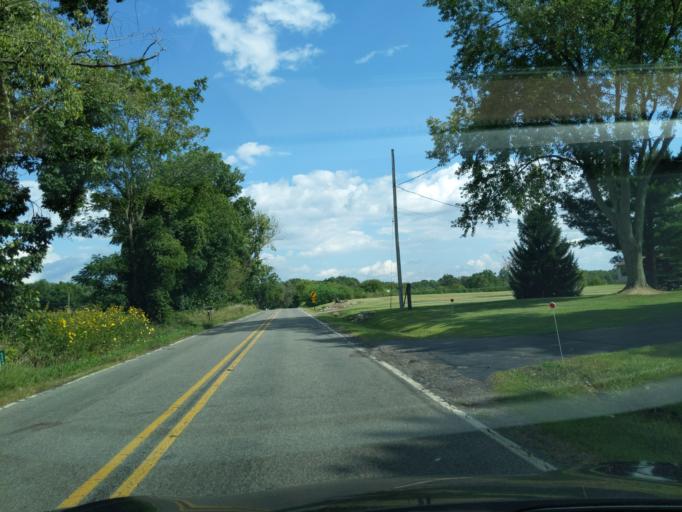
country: US
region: Michigan
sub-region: Jackson County
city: Jackson
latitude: 42.2949
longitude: -84.4865
